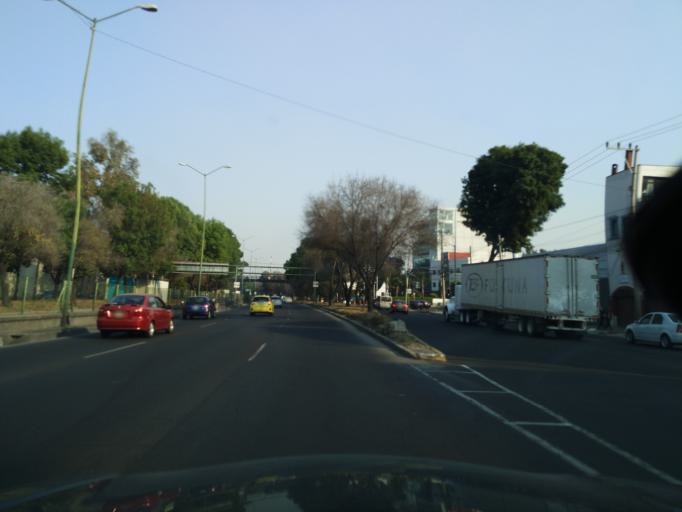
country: MX
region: Mexico City
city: Tlalpan
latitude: 19.2843
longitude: -99.1460
